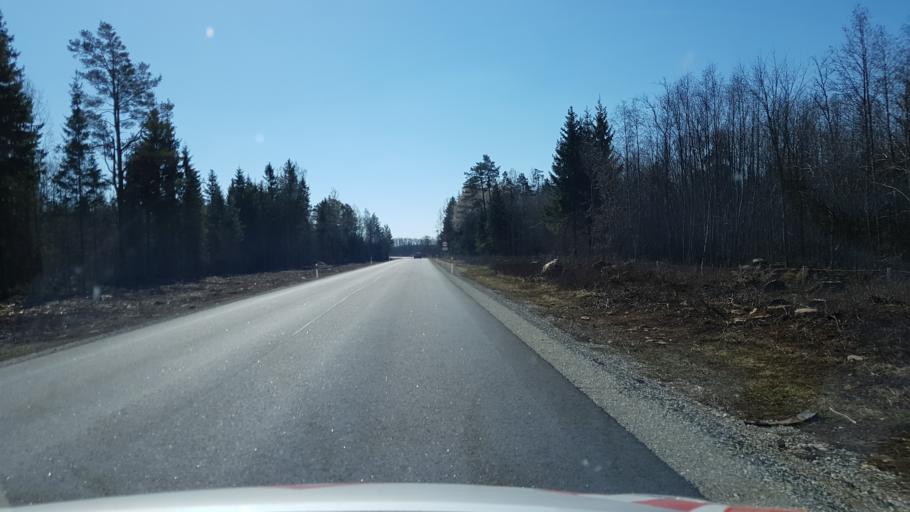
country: EE
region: Laeaene-Virumaa
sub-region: Vinni vald
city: Vinni
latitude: 59.0673
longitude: 26.6378
